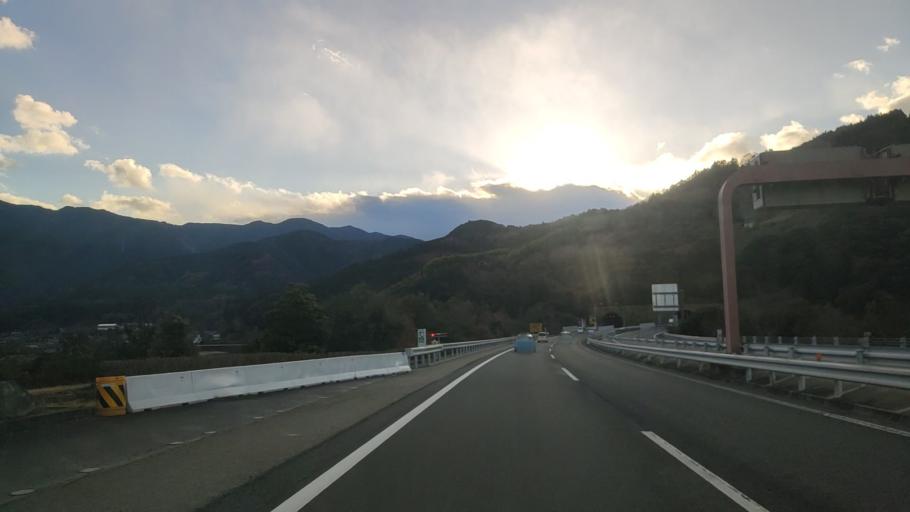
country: JP
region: Ehime
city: Saijo
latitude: 33.8772
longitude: 133.0816
